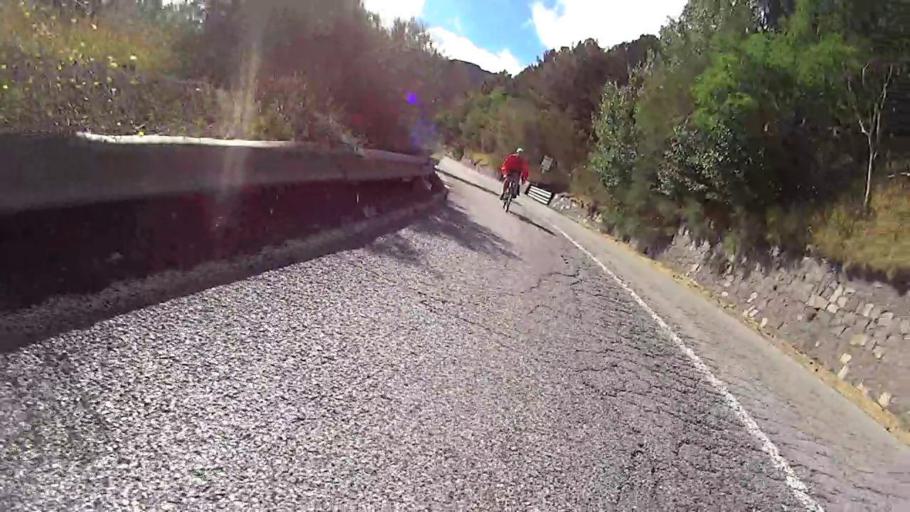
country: IT
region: Sicily
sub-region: Catania
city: Nicolosi
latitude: 37.7015
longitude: 15.0144
